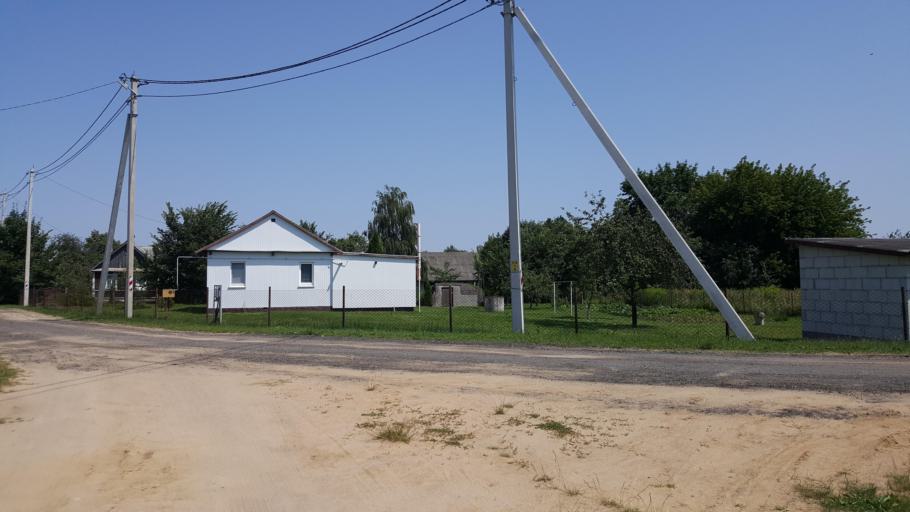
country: BY
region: Brest
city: Zhabinka
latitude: 52.1939
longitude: 23.9931
